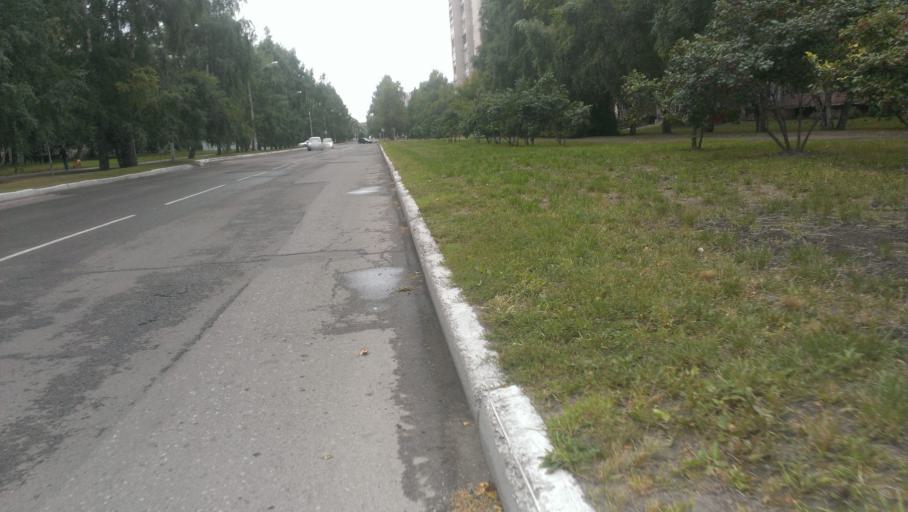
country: RU
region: Altai Krai
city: Novosilikatnyy
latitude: 53.3709
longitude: 83.6694
